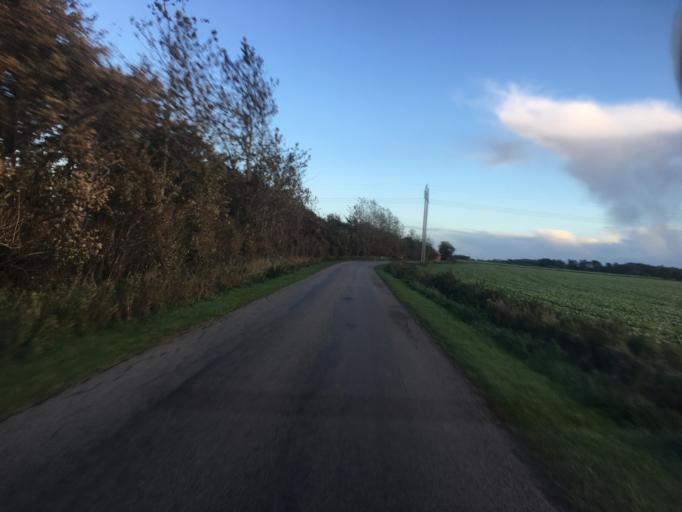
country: DE
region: Schleswig-Holstein
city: Ellhoft
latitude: 54.9554
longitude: 9.0183
